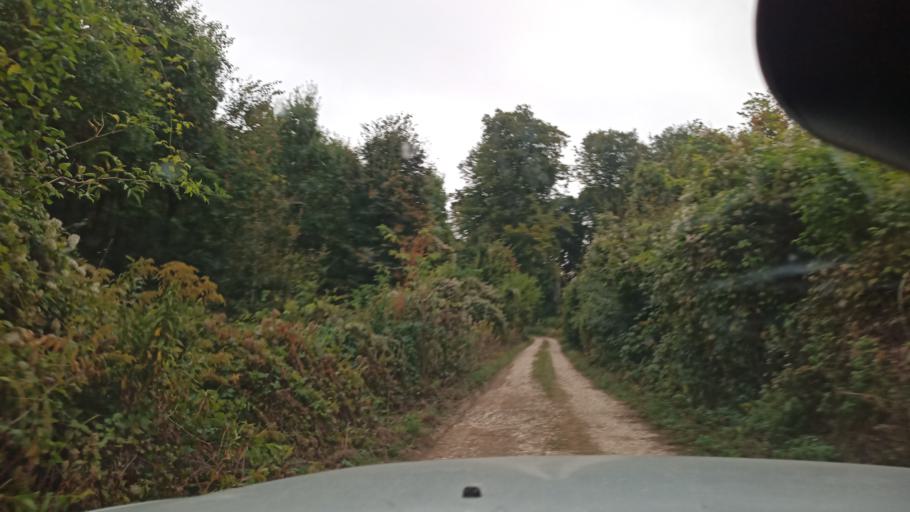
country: HU
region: Fejer
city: Mor
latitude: 47.3855
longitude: 18.2511
